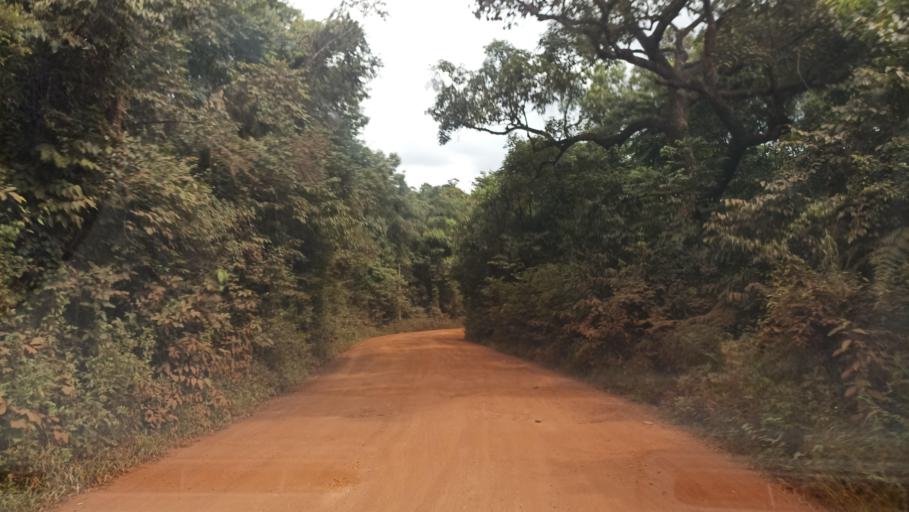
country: BR
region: Minas Gerais
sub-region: Itabirito
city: Itabirito
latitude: -20.3806
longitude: -43.7601
